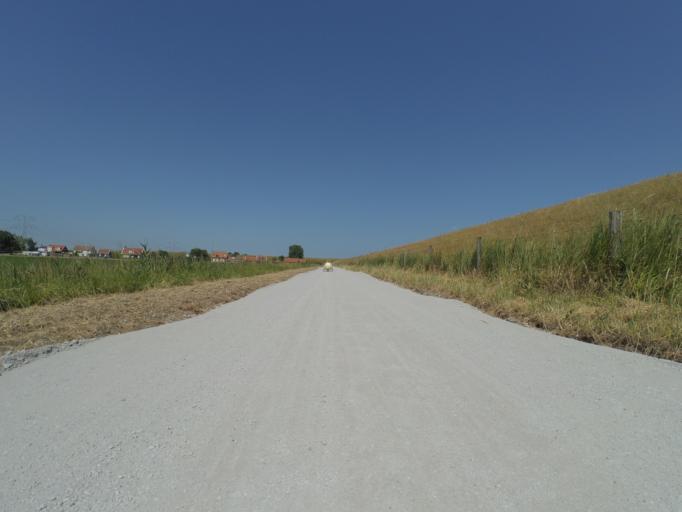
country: NL
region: Zeeland
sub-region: Gemeente Reimerswaal
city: Yerseke
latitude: 51.4342
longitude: 4.1300
